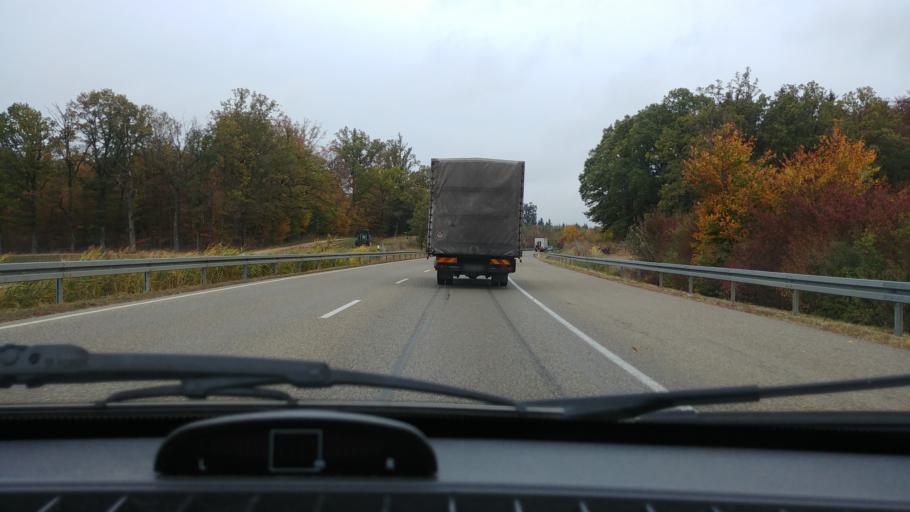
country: DE
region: Baden-Wuerttemberg
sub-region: Regierungsbezirk Stuttgart
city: Aalen
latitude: 48.8513
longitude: 10.0699
